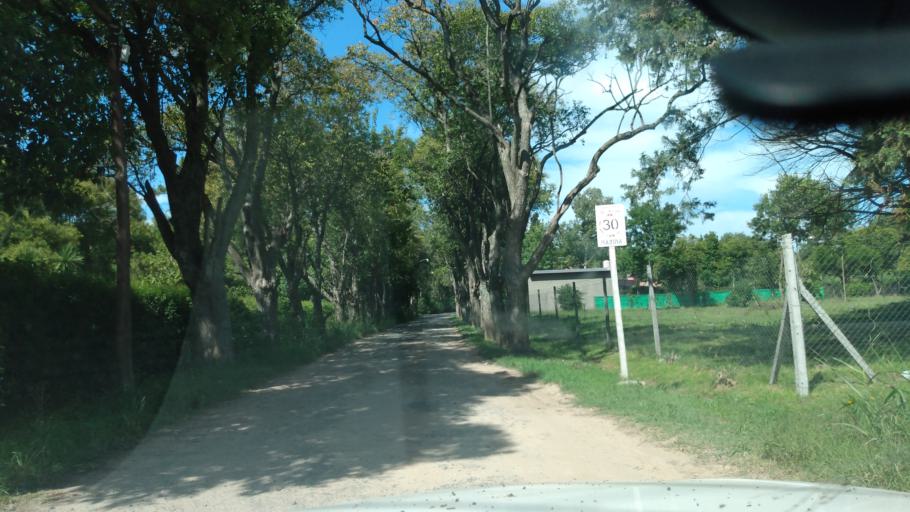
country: AR
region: Buenos Aires
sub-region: Partido de Lujan
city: Lujan
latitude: -34.5490
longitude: -59.1482
